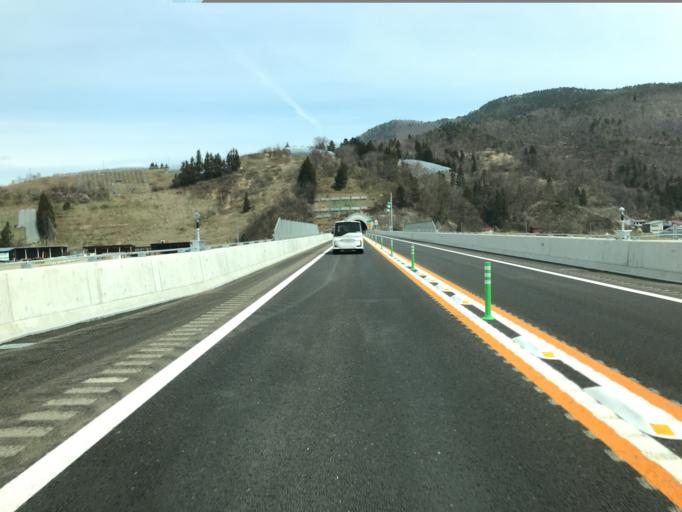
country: JP
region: Yamagata
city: Takahata
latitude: 38.0403
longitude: 140.1882
